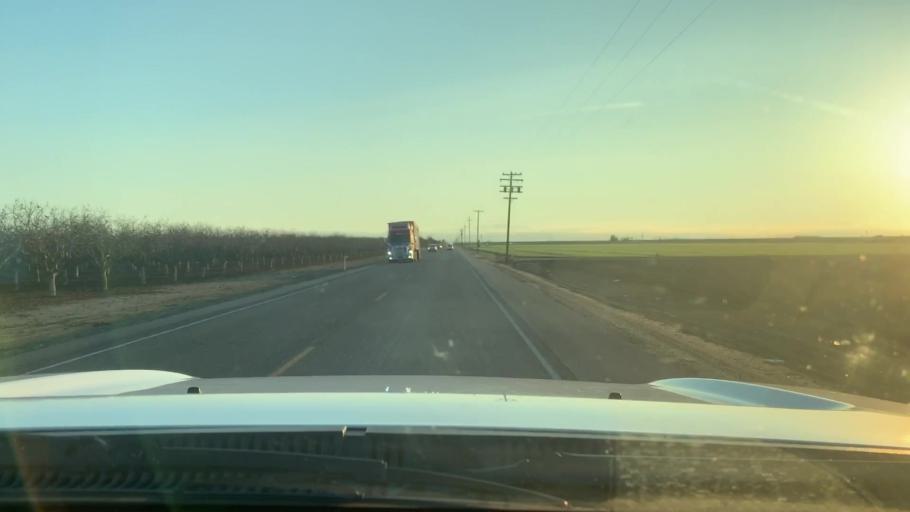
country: US
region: California
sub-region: Kern County
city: Shafter
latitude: 35.5001
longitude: -119.3645
